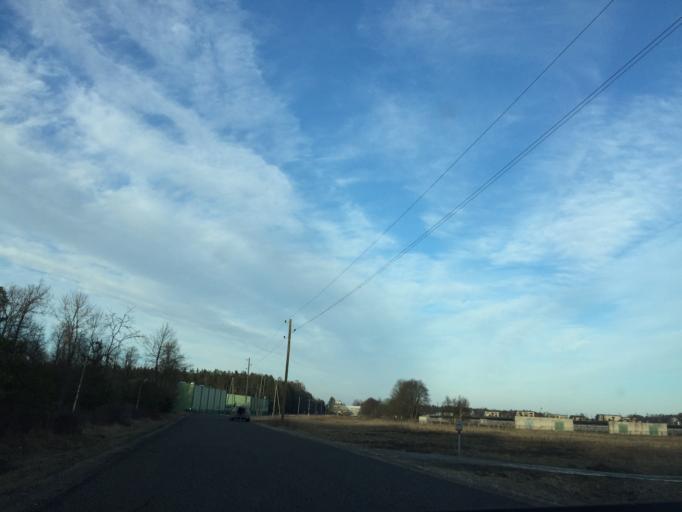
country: LV
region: Kekava
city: Kekava
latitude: 56.8233
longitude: 24.1895
